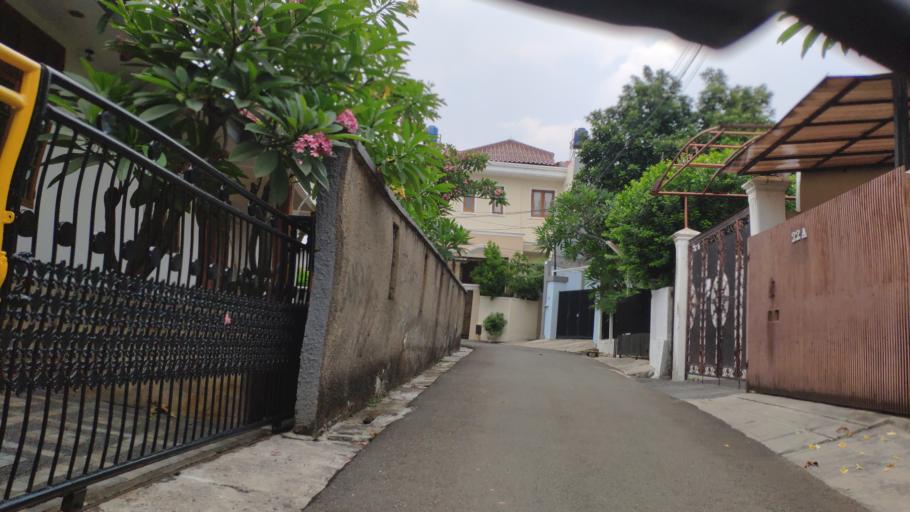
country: ID
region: Jakarta Raya
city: Jakarta
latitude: -6.2703
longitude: 106.7950
